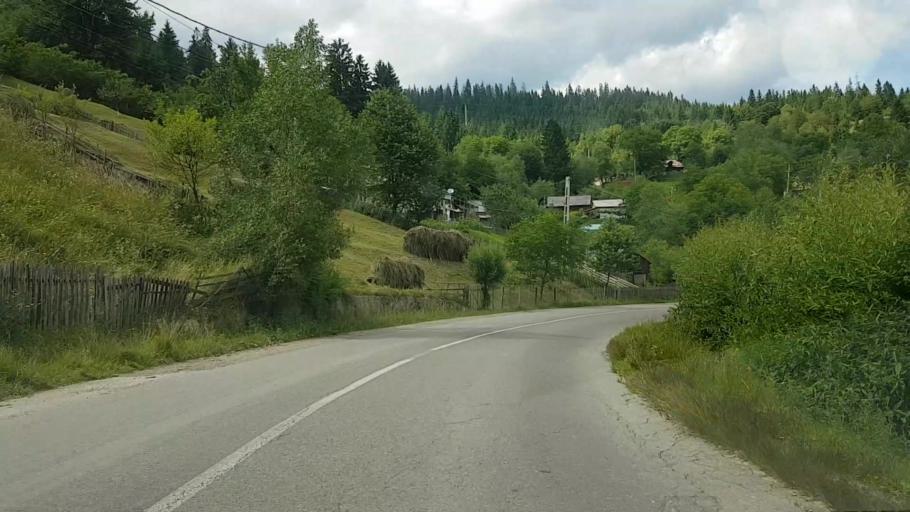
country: RO
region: Neamt
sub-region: Comuna Hangu
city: Hangu
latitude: 47.0527
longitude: 26.0236
